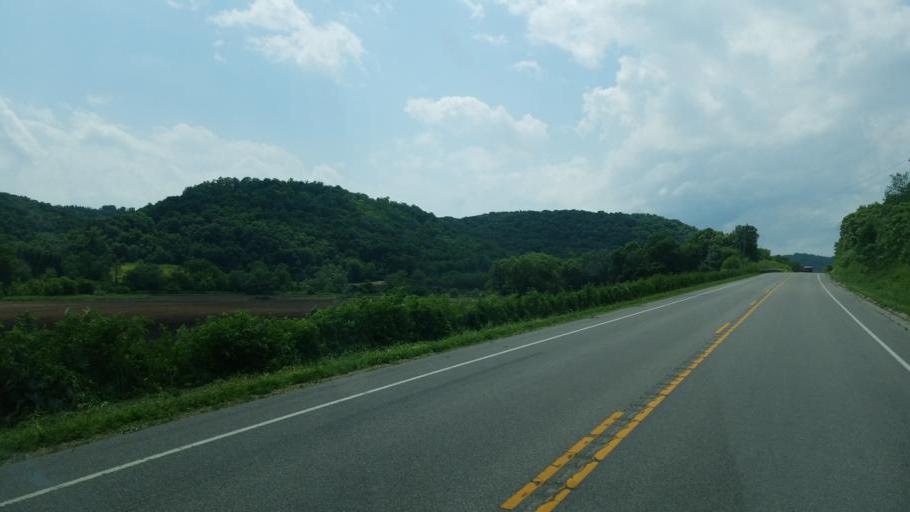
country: US
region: Wisconsin
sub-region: Vernon County
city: Viroqua
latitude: 43.4664
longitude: -90.7202
